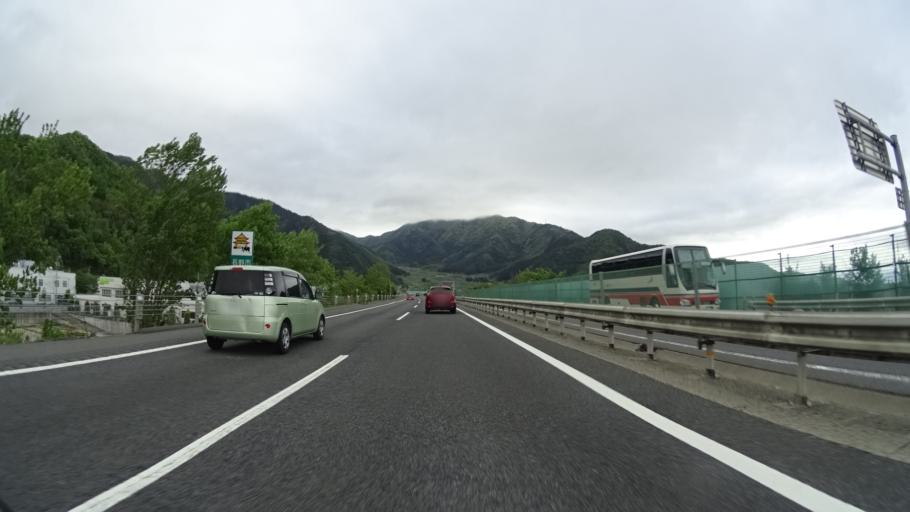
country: JP
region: Nagano
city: Suzaka
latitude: 36.6310
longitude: 138.2730
